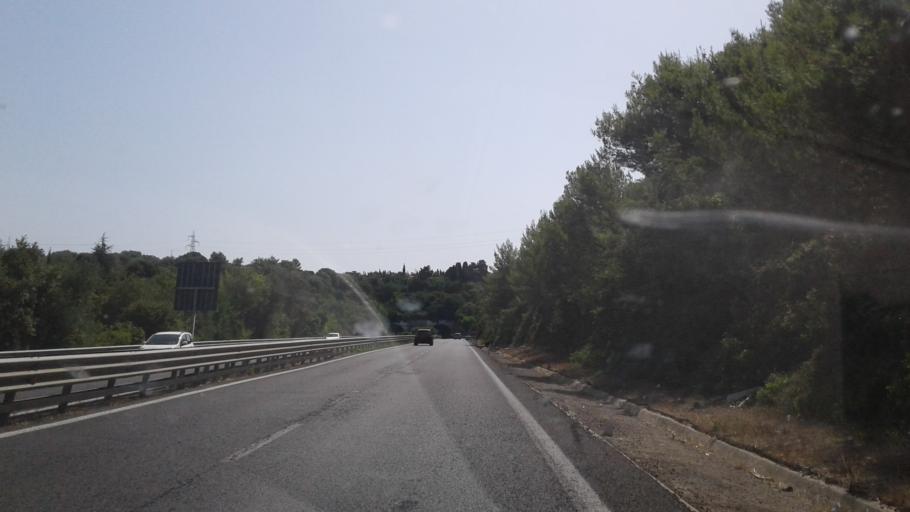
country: IT
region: Sardinia
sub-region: Provincia di Sassari
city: Tissi
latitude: 40.6982
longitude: 8.5646
